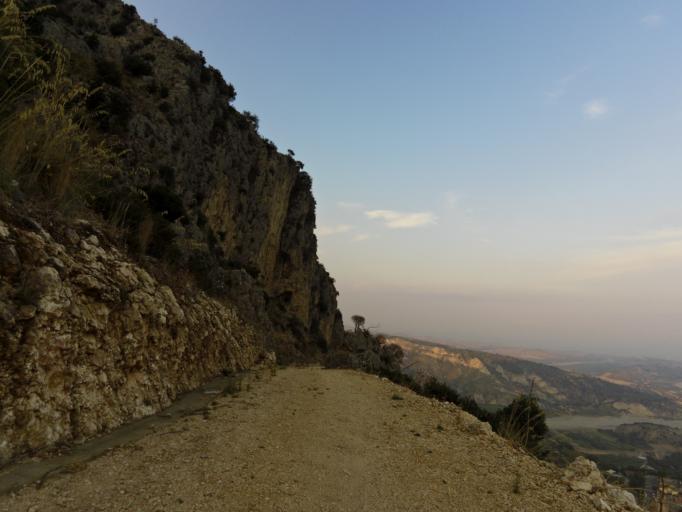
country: IT
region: Calabria
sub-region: Provincia di Reggio Calabria
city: Stilo
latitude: 38.4791
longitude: 16.4634
